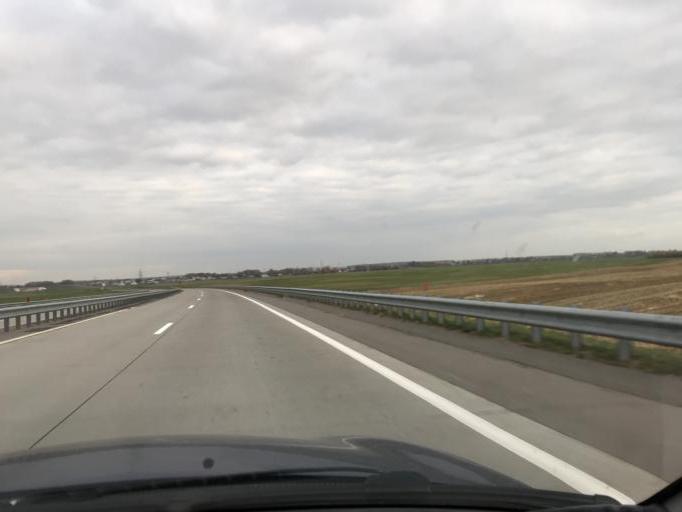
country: BY
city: Fanipol
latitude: 53.7656
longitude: 27.3712
